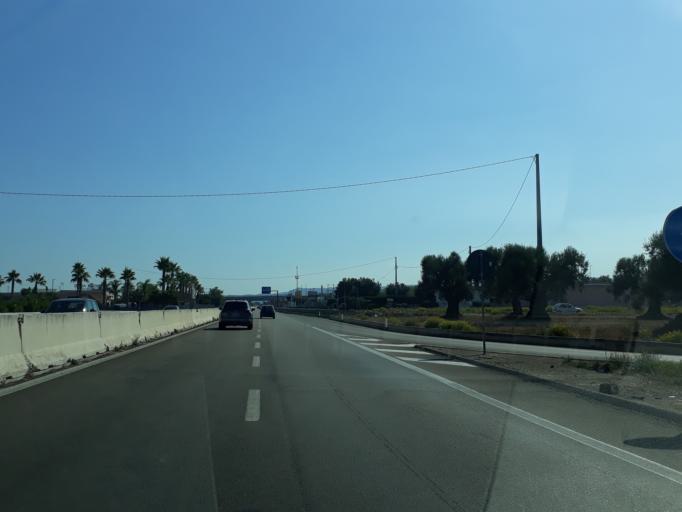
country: IT
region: Apulia
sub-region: Provincia di Brindisi
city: Fasano
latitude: 40.8547
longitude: 17.3534
